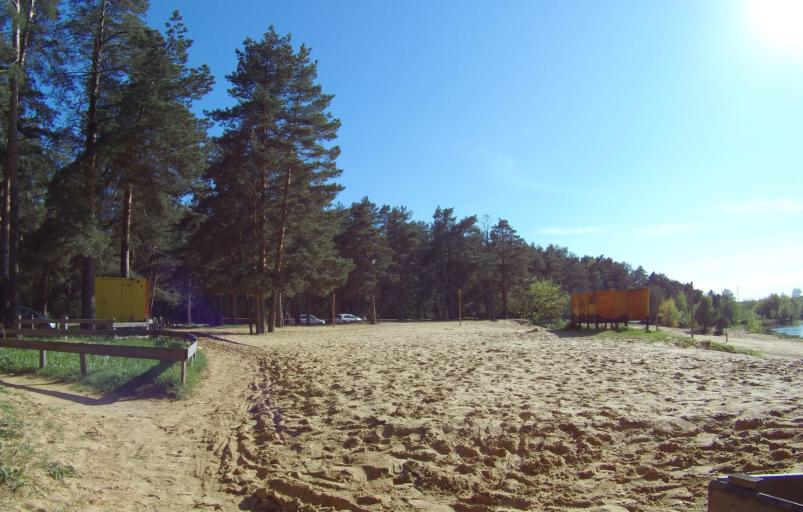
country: RU
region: Moskovskaya
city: Kratovo
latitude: 55.5660
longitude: 38.1839
